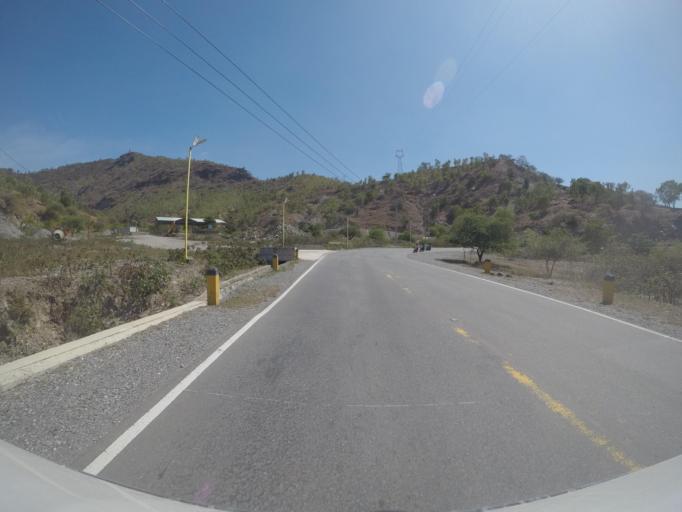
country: TL
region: Liquica
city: Liquica
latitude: -8.5747
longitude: 125.3750
